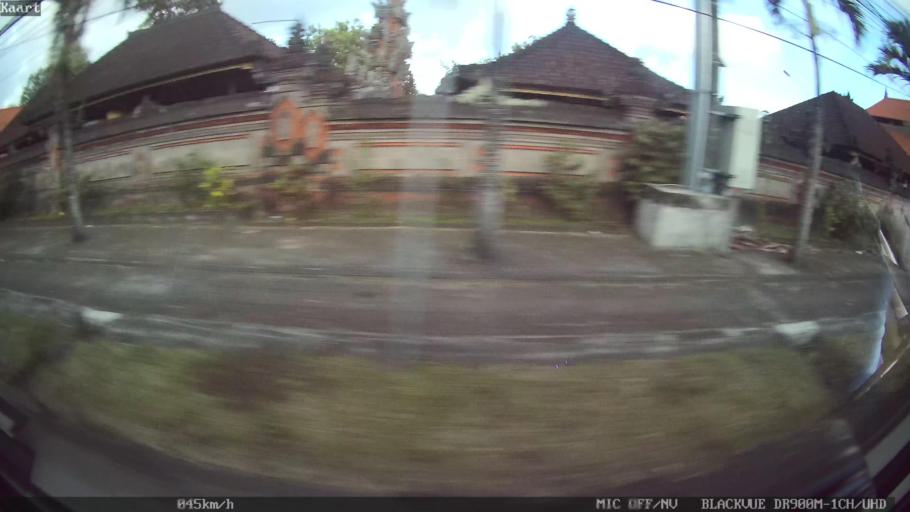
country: ID
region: Bali
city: Banjar Parekan
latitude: -8.5687
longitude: 115.2198
